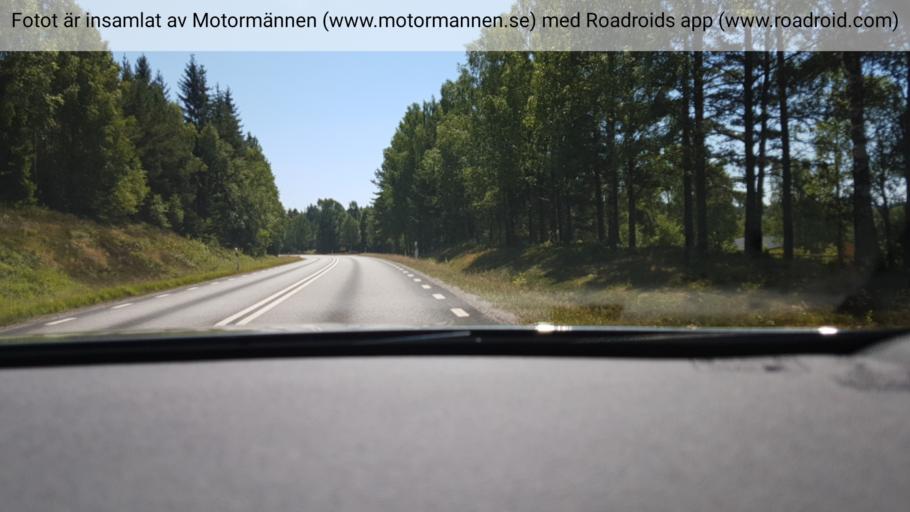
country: SE
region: Joenkoeping
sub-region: Gnosjo Kommun
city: Gnosjoe
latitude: 57.3567
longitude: 13.7513
